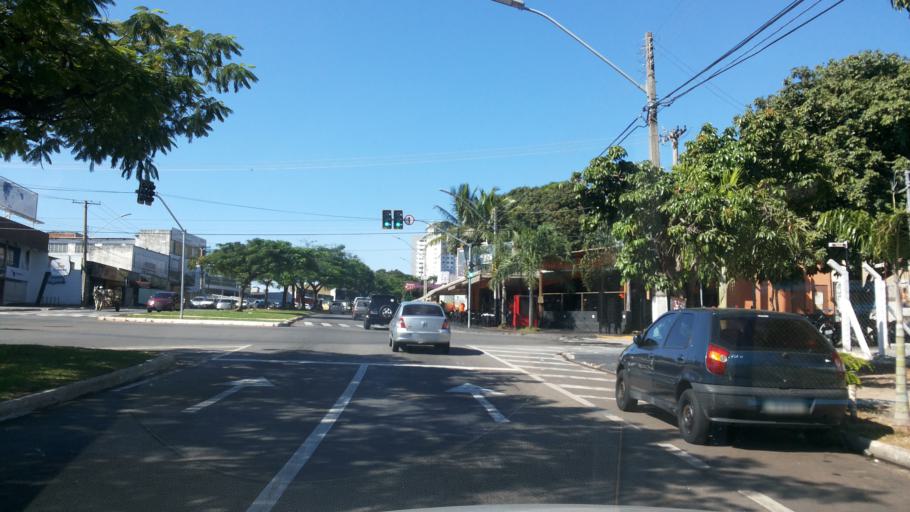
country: BR
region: Goias
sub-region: Goiania
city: Goiania
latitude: -16.7090
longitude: -49.2515
